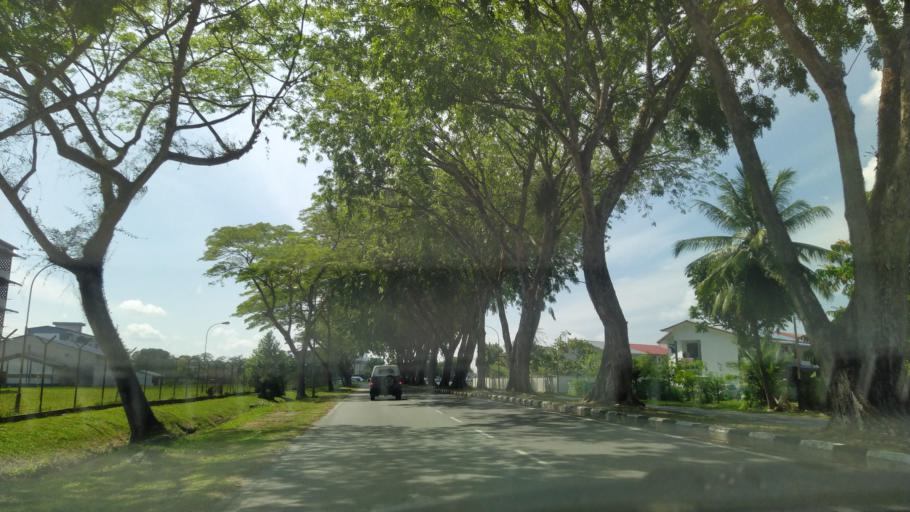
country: MY
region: Sarawak
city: Sibu
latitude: 2.3123
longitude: 111.8338
